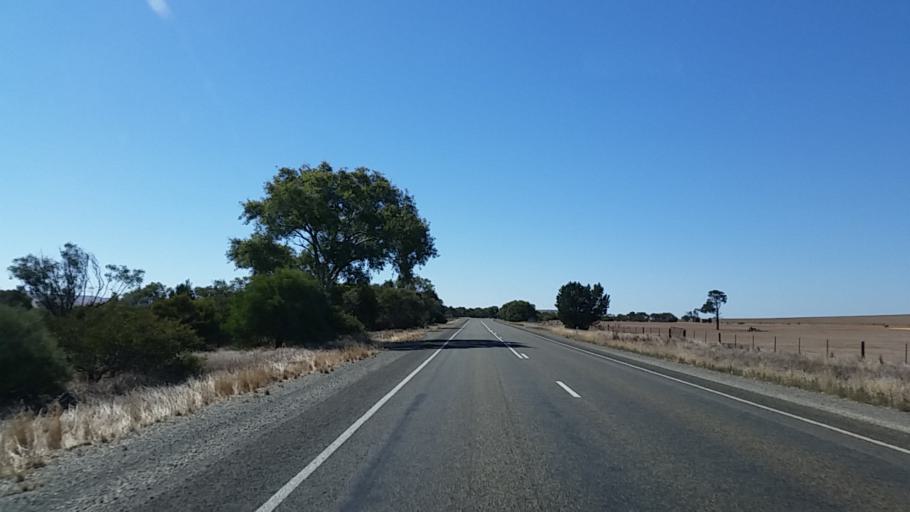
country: AU
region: South Australia
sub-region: Northern Areas
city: Jamestown
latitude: -33.2460
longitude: 138.8739
